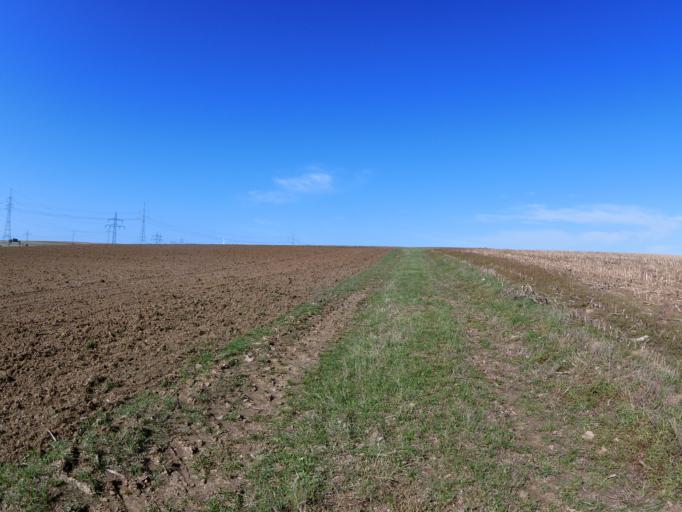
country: DE
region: Bavaria
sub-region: Regierungsbezirk Unterfranken
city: Biebelried
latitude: 49.7609
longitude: 10.0635
